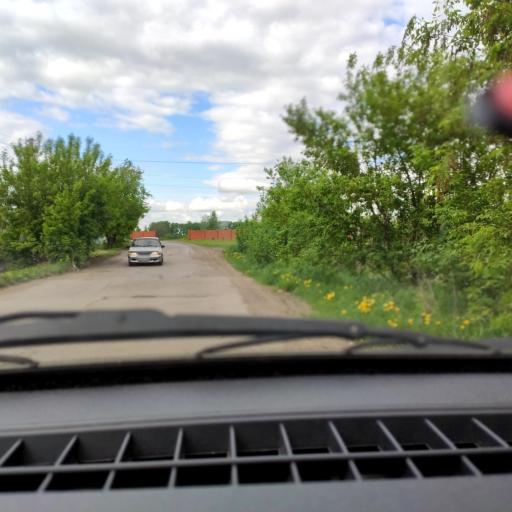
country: RU
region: Bashkortostan
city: Ufa
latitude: 54.5431
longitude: 55.9202
